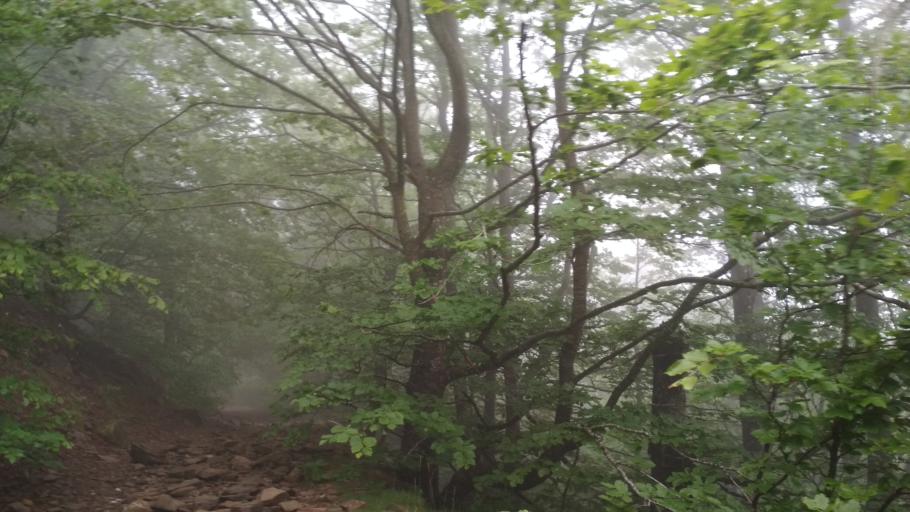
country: ES
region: Catalonia
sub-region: Provincia de Barcelona
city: Fogars de Montclus
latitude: 41.7748
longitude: 2.4456
